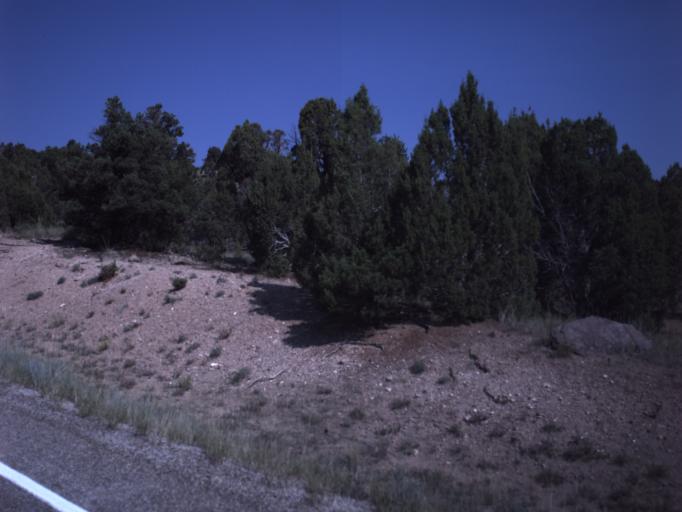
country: US
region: Utah
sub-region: Daggett County
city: Manila
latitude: 40.9096
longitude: -109.4379
